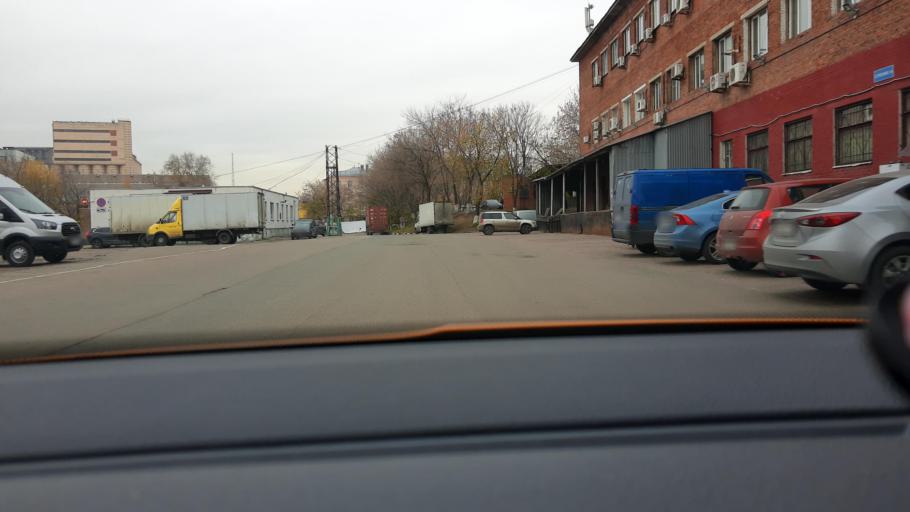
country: RU
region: Moskovskaya
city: Presnenskiy
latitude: 55.7703
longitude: 37.5285
